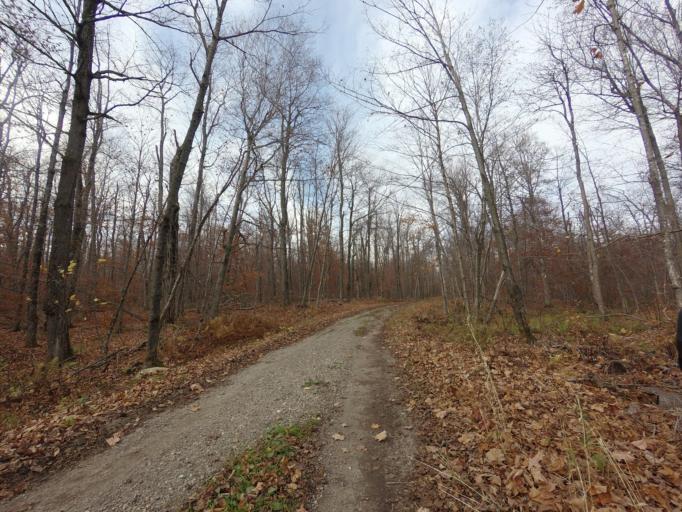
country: CA
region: Quebec
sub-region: Outaouais
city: Wakefield
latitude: 45.5465
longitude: -75.9665
